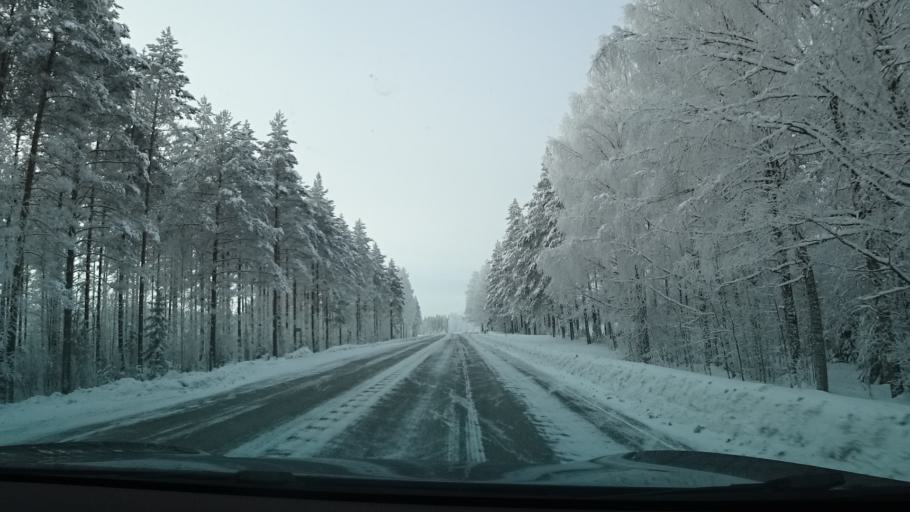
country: FI
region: South Karelia
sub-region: Imatra
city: Saari
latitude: 61.7803
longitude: 29.7044
